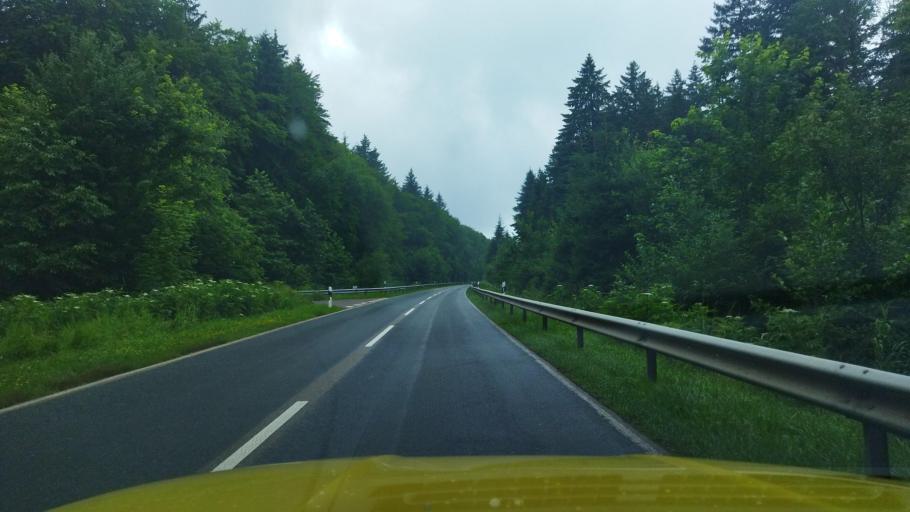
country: DE
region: Bavaria
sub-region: Lower Bavaria
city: Riedenburg
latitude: 48.9440
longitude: 11.6644
